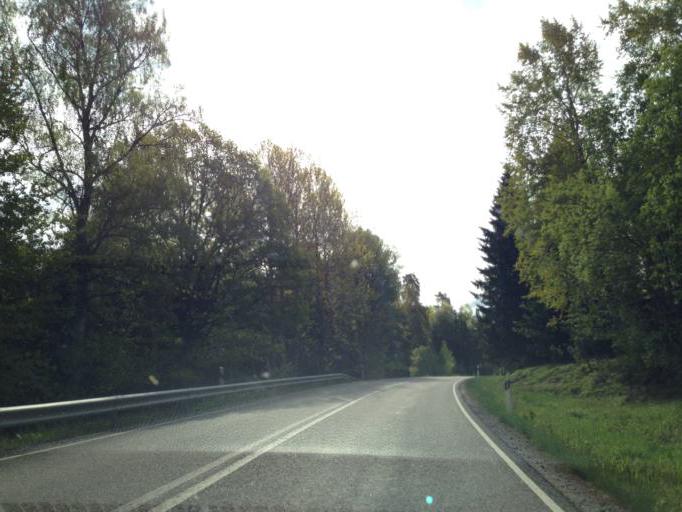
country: SE
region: Soedermanland
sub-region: Nykopings Kommun
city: Stigtomta
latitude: 58.9716
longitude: 16.8502
